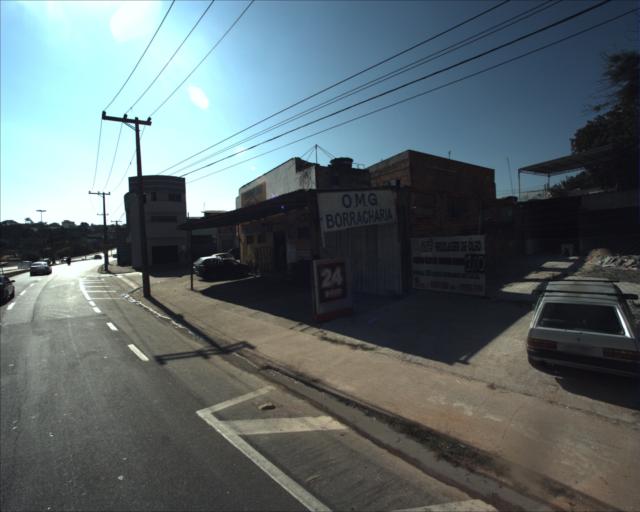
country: BR
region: Sao Paulo
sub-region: Sorocaba
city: Sorocaba
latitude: -23.4900
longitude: -47.4949
